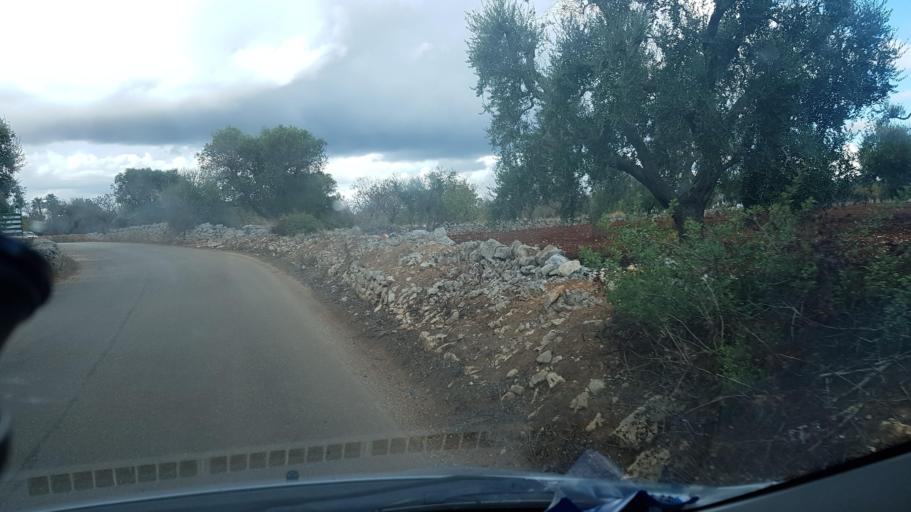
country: IT
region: Apulia
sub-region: Provincia di Brindisi
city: San Vito dei Normanni
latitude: 40.6528
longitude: 17.7254
